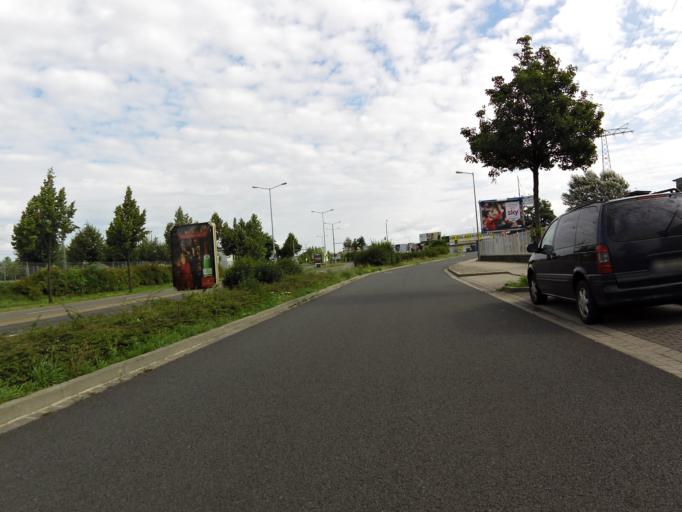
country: DE
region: Saxony
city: Leipzig
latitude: 51.3572
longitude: 12.3975
